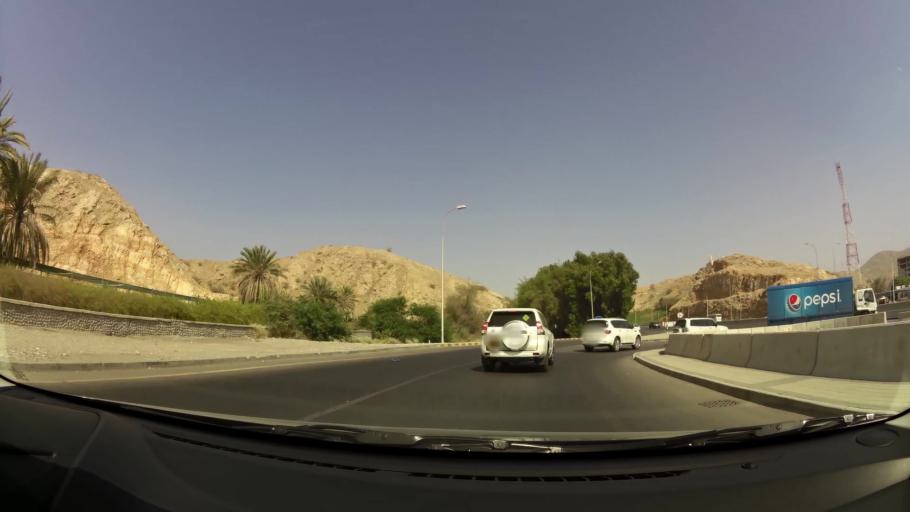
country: OM
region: Muhafazat Masqat
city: Muscat
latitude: 23.6084
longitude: 58.5013
